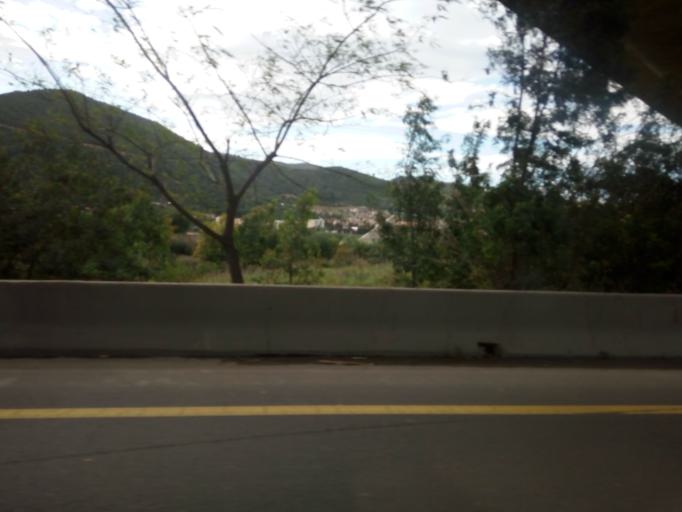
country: DZ
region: Tipaza
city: El Affroun
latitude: 36.4194
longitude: 2.5652
